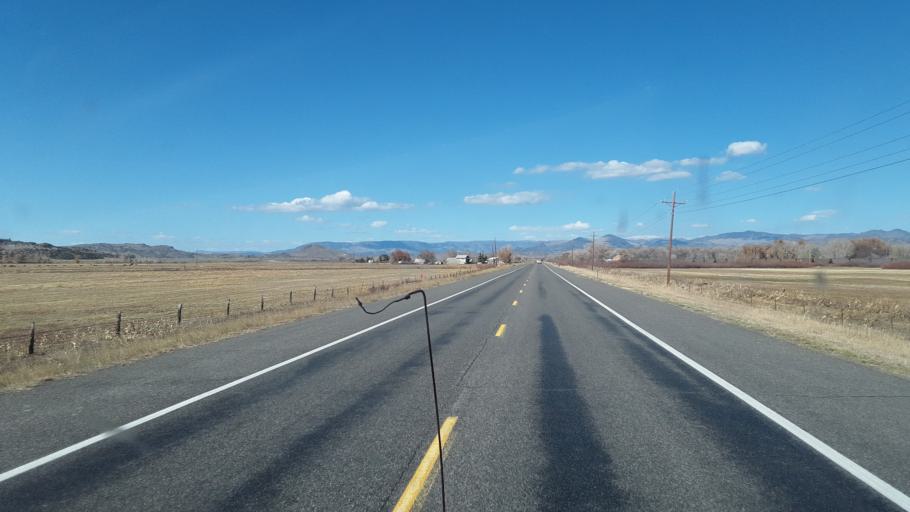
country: US
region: Colorado
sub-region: Rio Grande County
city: Del Norte
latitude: 37.6520
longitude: -106.2795
